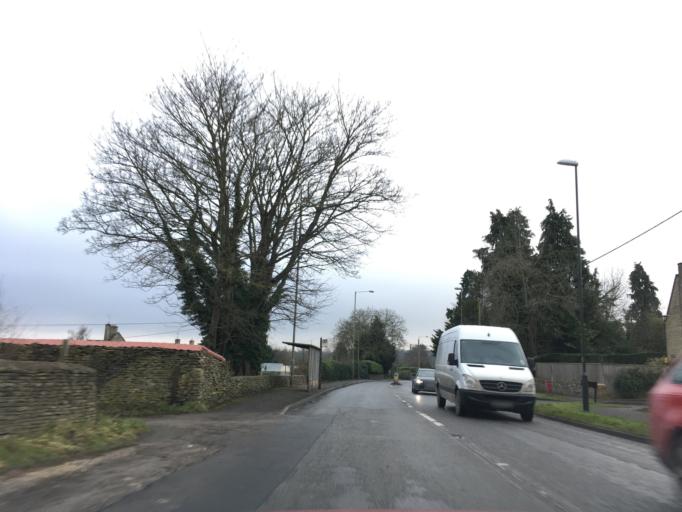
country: GB
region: England
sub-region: Gloucestershire
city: Cirencester
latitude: 51.7307
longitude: -1.9736
